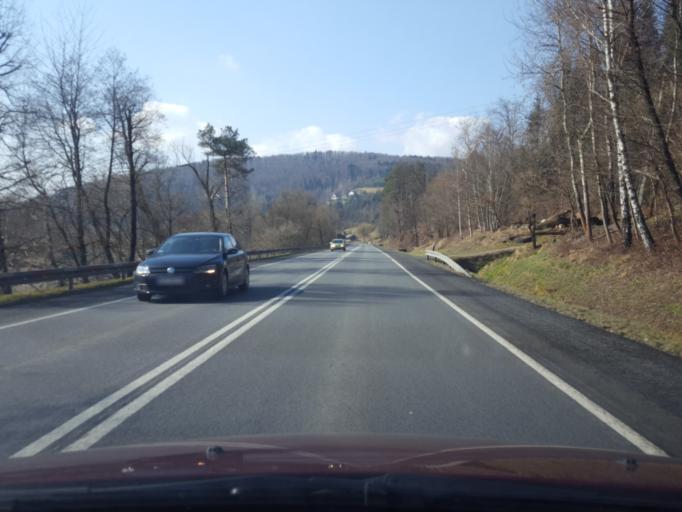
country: PL
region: Lesser Poland Voivodeship
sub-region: Powiat nowosadecki
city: Lososina Dolna
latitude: 49.7844
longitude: 20.6471
